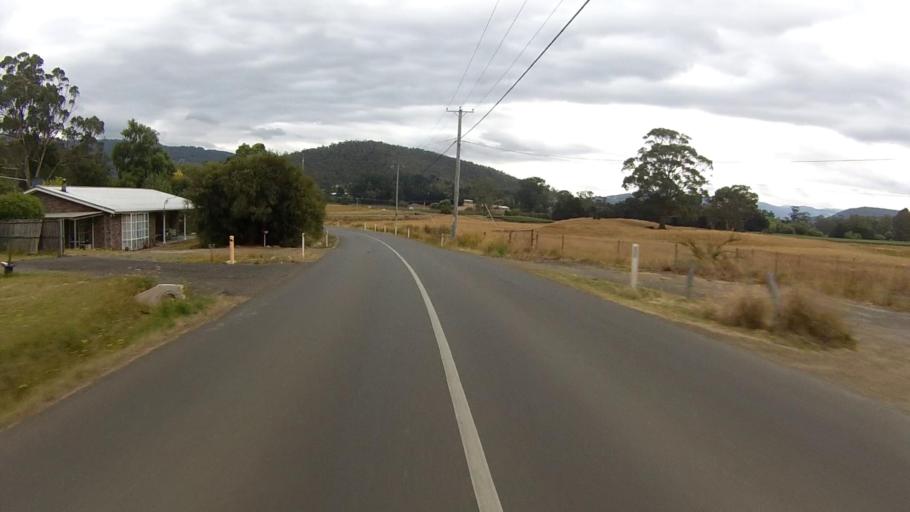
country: AU
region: Tasmania
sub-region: Huon Valley
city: Huonville
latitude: -42.9803
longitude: 147.0965
